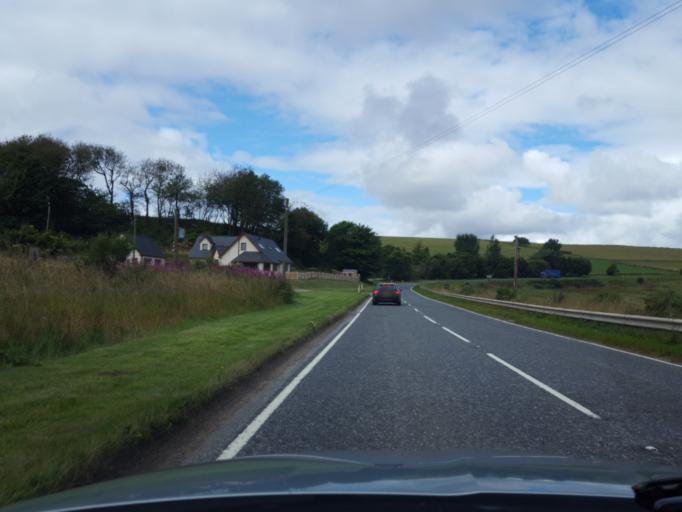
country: GB
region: Scotland
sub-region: Moray
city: Rothes
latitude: 57.5350
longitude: -3.2173
